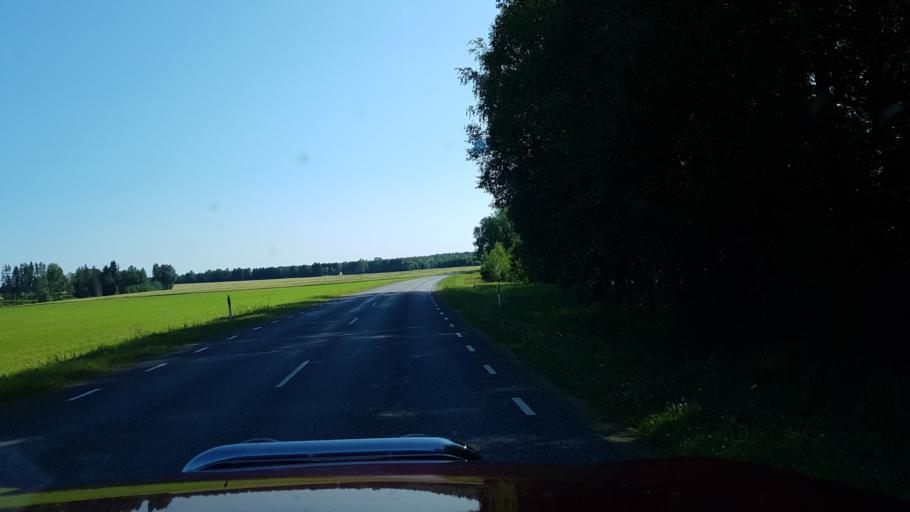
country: EE
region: Polvamaa
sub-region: Polva linn
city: Polva
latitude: 57.9977
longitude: 26.9136
